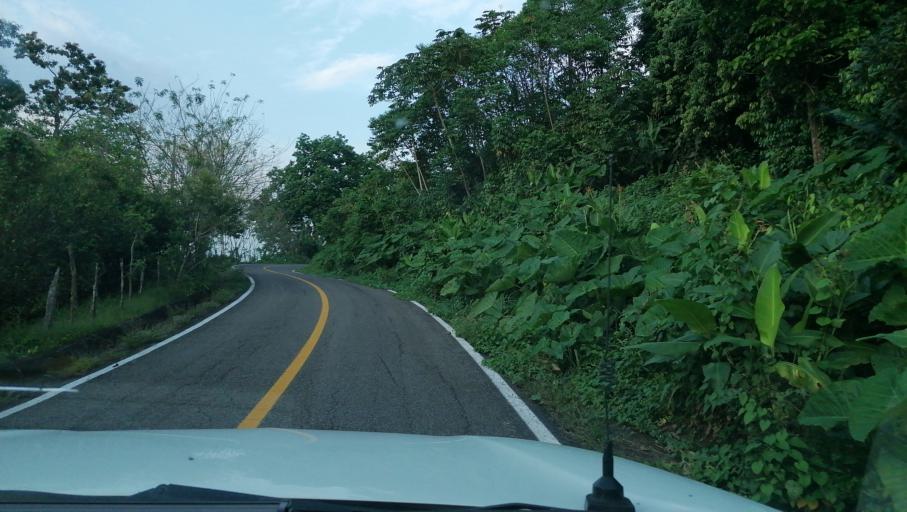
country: MX
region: Chiapas
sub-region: Juarez
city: El Triunfo 1ra. Seccion (Cardona)
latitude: 17.5059
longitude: -93.2338
